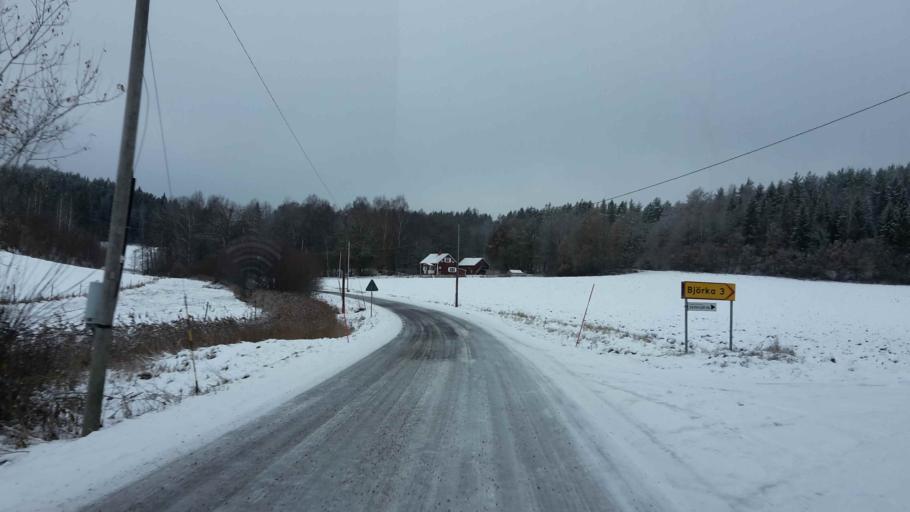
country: SE
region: Kalmar
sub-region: Vasterviks Kommun
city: Overum
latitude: 58.1536
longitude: 16.3041
